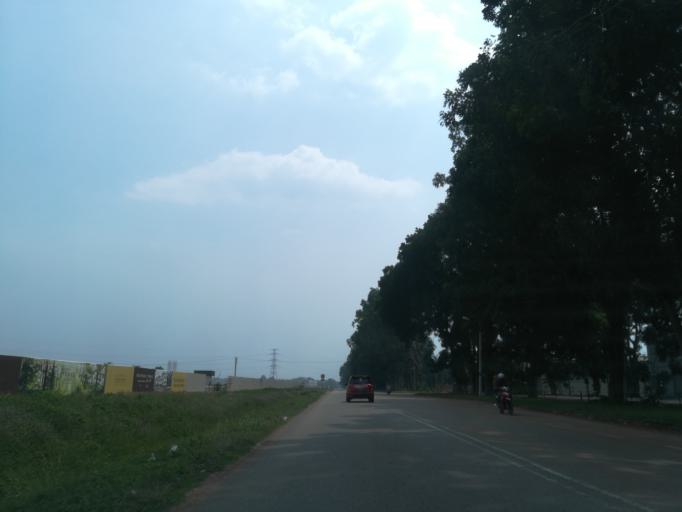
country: MY
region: Penang
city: Tasek Glugor
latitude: 5.4474
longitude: 100.5386
